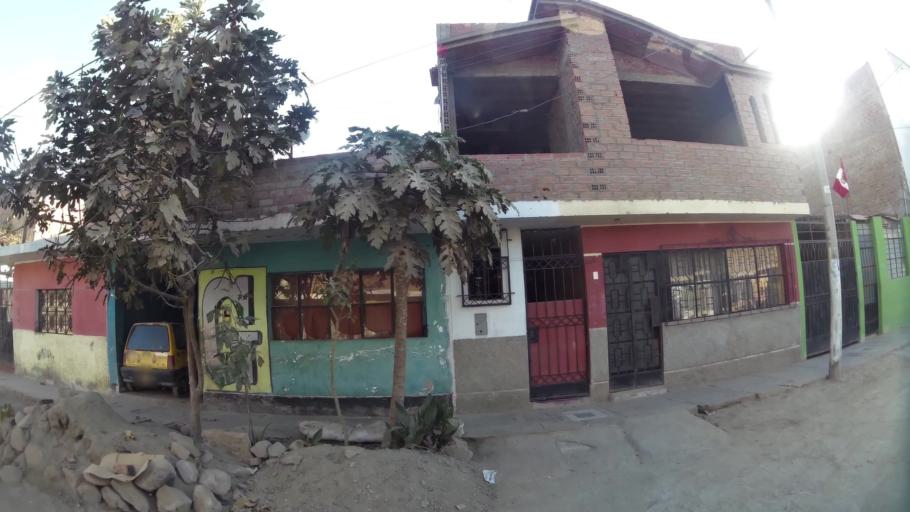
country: PE
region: Ica
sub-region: Provincia de Ica
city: Ica
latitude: -14.0685
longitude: -75.7195
